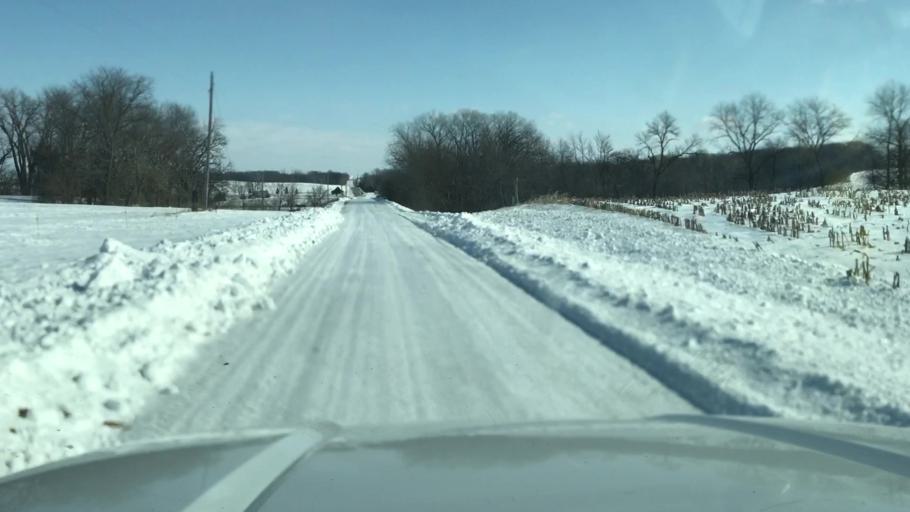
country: US
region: Missouri
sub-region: Nodaway County
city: Maryville
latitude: 40.3865
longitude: -94.6711
